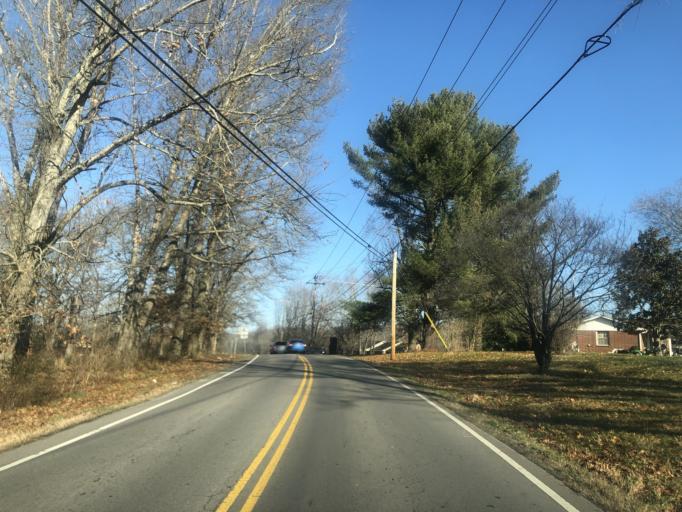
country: US
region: Tennessee
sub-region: Williamson County
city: Nolensville
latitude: 36.0243
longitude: -86.6645
